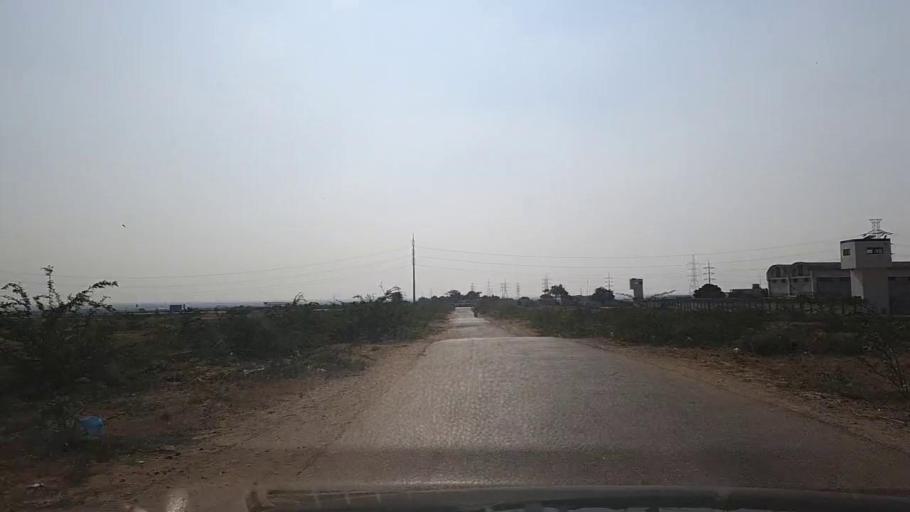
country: PK
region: Sindh
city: Gharo
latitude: 24.7688
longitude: 67.5529
